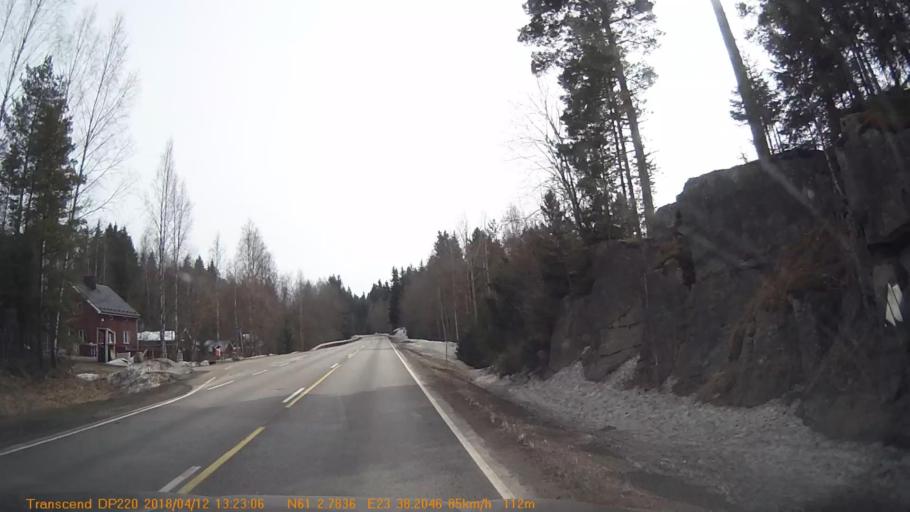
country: FI
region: Pirkanmaa
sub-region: Etelae-Pirkanmaa
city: Urjala
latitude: 61.0453
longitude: 23.6378
